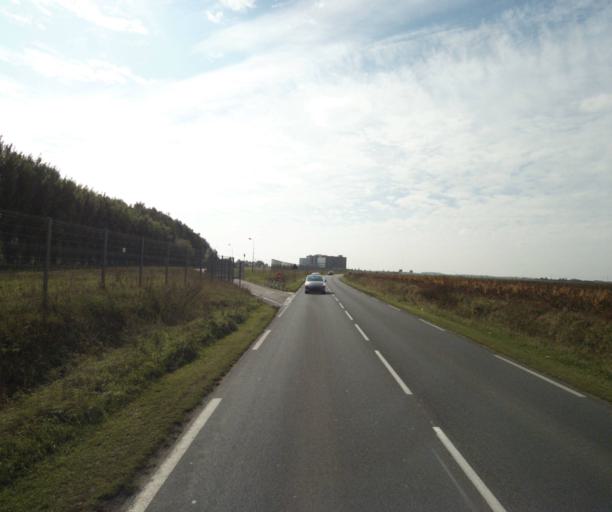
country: FR
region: Nord-Pas-de-Calais
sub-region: Departement du Nord
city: Wattignies
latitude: 50.5728
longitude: 3.0268
